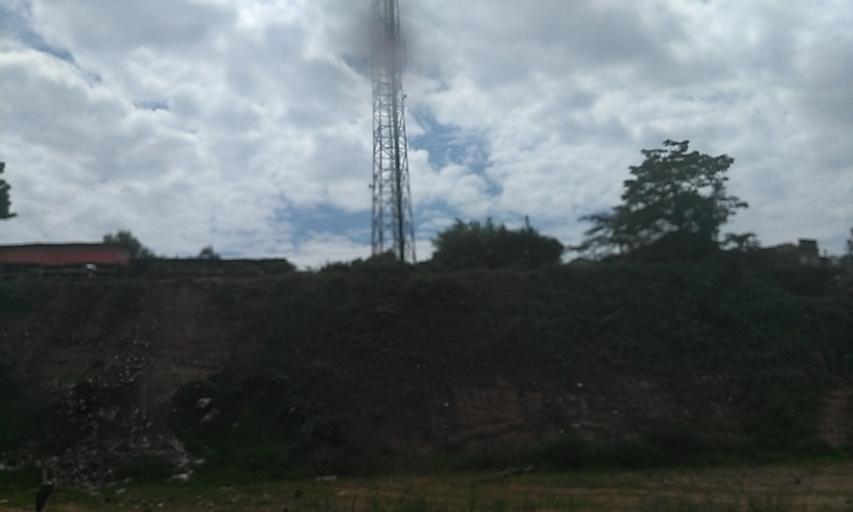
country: UG
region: Central Region
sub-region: Wakiso District
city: Kireka
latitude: 0.3614
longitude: 32.6370
